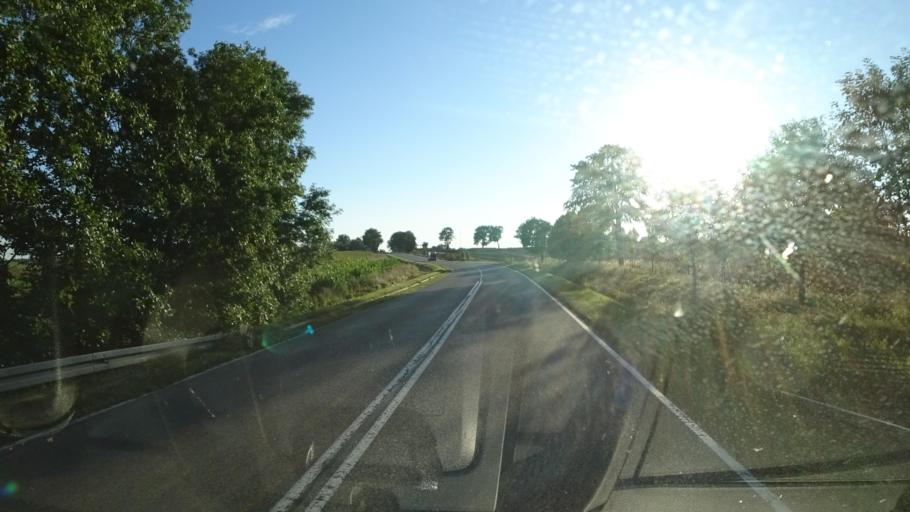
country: PL
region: Warmian-Masurian Voivodeship
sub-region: Powiat olecki
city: Olecko
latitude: 53.8624
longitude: 22.5476
